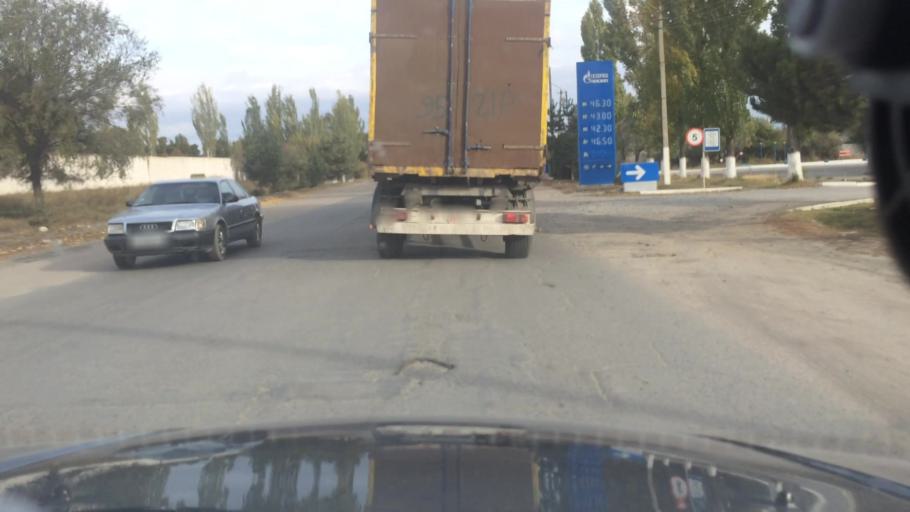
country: KG
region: Ysyk-Koel
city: Karakol
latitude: 42.5159
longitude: 78.3858
